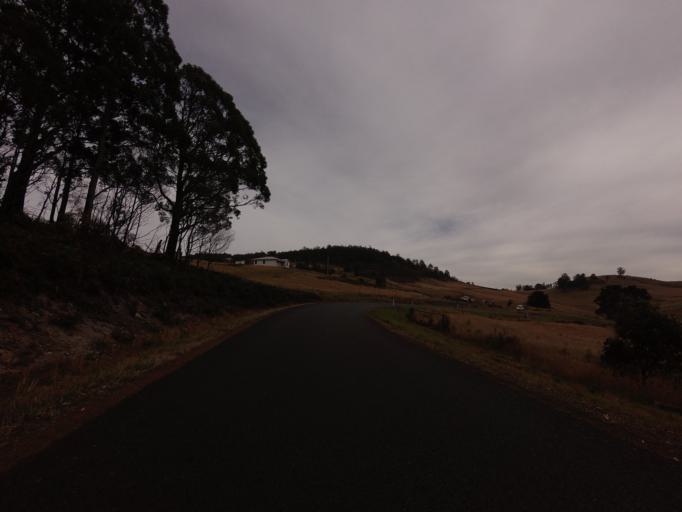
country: AU
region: Tasmania
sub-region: Sorell
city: Sorell
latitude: -42.4881
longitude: 147.5644
